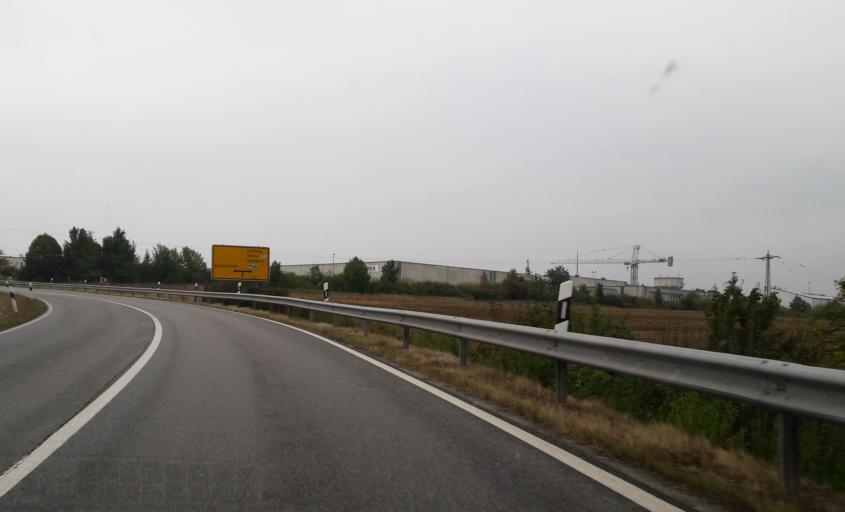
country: DE
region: Rheinland-Pfalz
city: Zweibrucken
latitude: 49.2352
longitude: 7.3973
